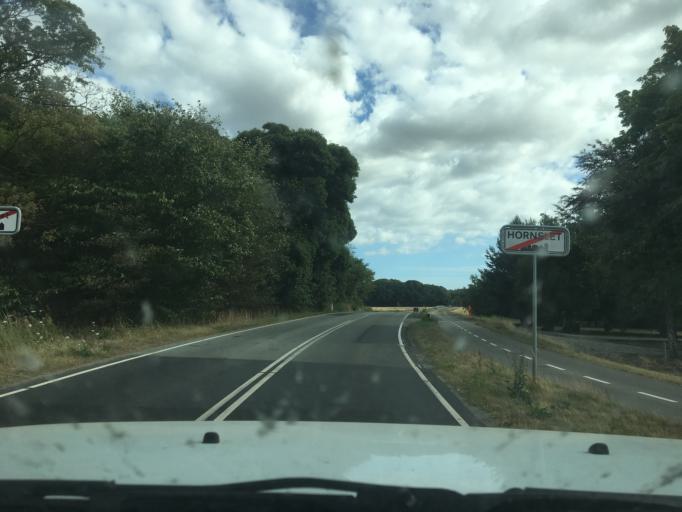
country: DK
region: Central Jutland
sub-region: Syddjurs Kommune
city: Hornslet
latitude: 56.3046
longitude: 10.3169
